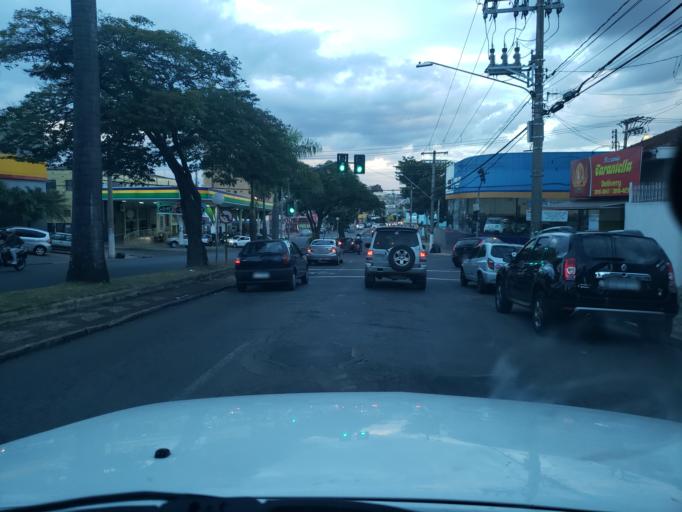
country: BR
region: Sao Paulo
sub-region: Moji-Guacu
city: Mogi-Gaucu
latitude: -22.3638
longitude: -46.9453
